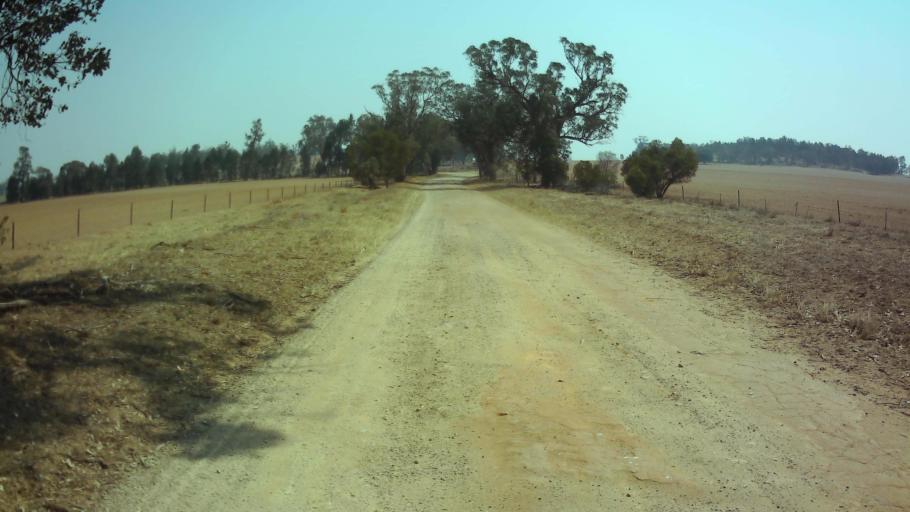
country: AU
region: New South Wales
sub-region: Weddin
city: Grenfell
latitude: -33.6486
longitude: 148.2700
